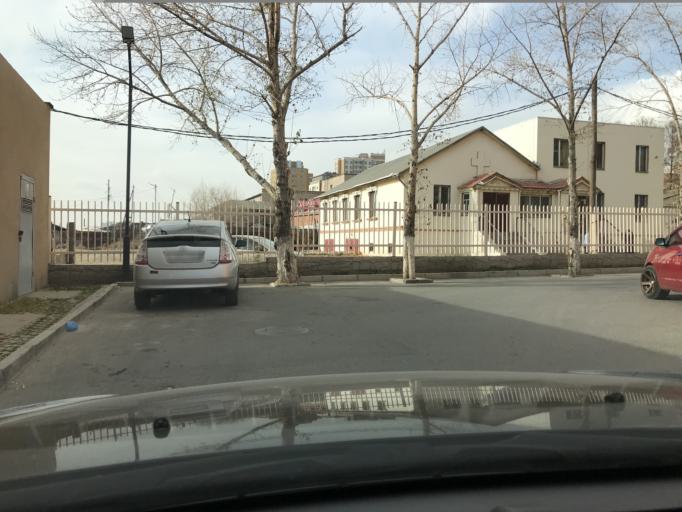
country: MN
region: Ulaanbaatar
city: Ulaanbaatar
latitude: 47.9145
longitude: 106.9677
